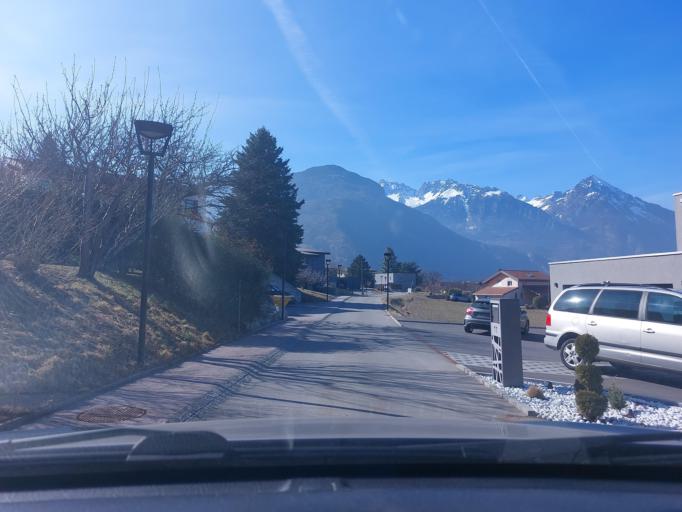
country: CH
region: Valais
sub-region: Martigny District
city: Martigny-Ville
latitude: 46.1034
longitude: 7.1000
